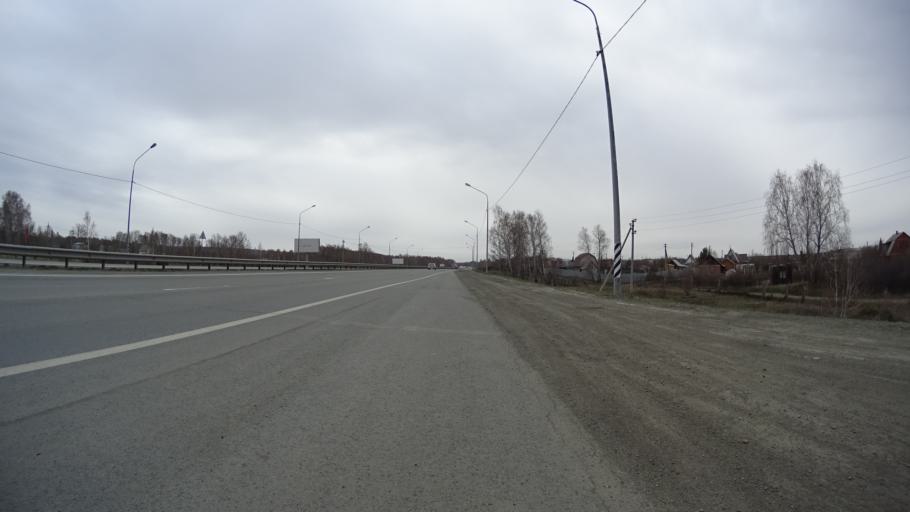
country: RU
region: Chelyabinsk
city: Novosineglazovskiy
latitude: 54.9794
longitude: 61.4153
